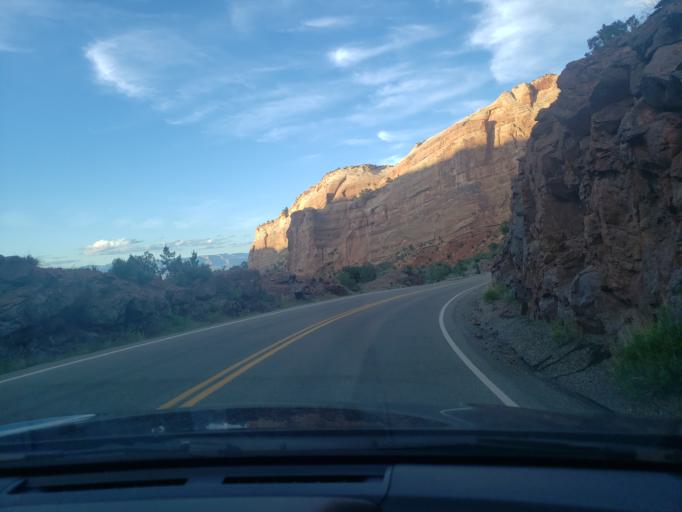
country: US
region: Colorado
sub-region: Mesa County
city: Fruita
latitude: 39.1090
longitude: -108.7348
